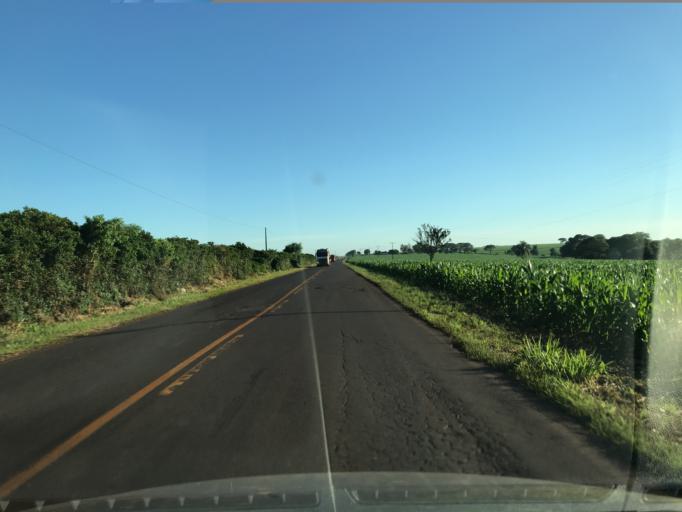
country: BR
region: Parana
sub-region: Palotina
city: Palotina
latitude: -24.1243
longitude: -53.8498
